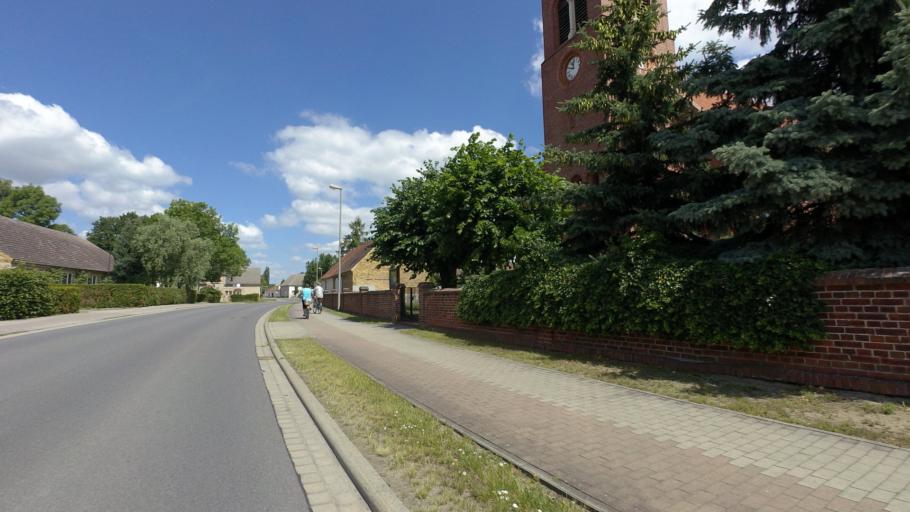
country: DE
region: Brandenburg
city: Sonnewalde
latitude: 51.6662
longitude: 13.6440
